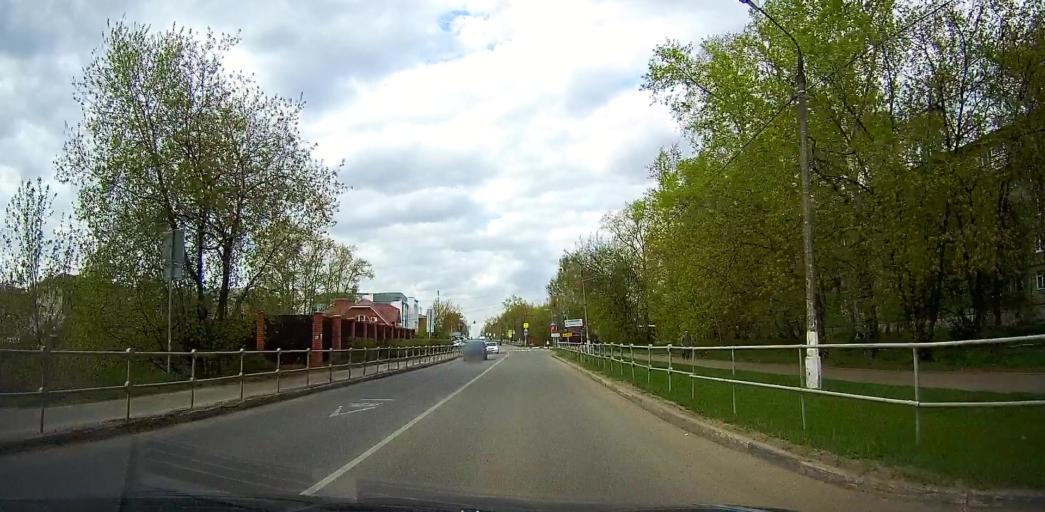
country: RU
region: Moskovskaya
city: Pavlovskiy Posad
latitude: 55.7685
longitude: 38.6555
